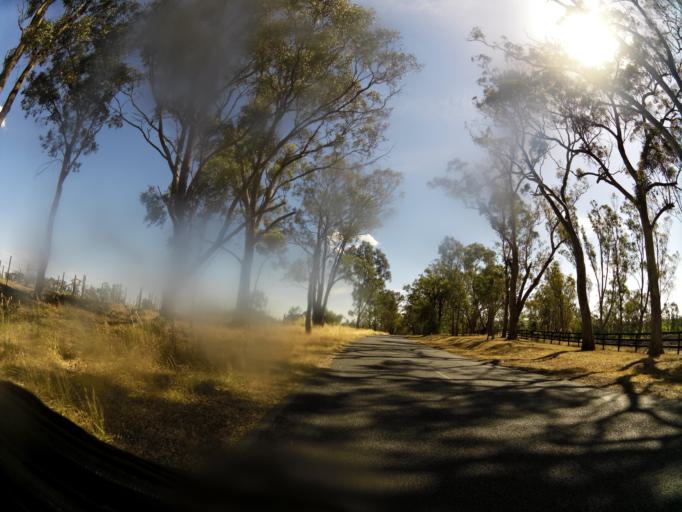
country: AU
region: Victoria
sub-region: Campaspe
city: Kyabram
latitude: -36.8566
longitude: 145.0962
